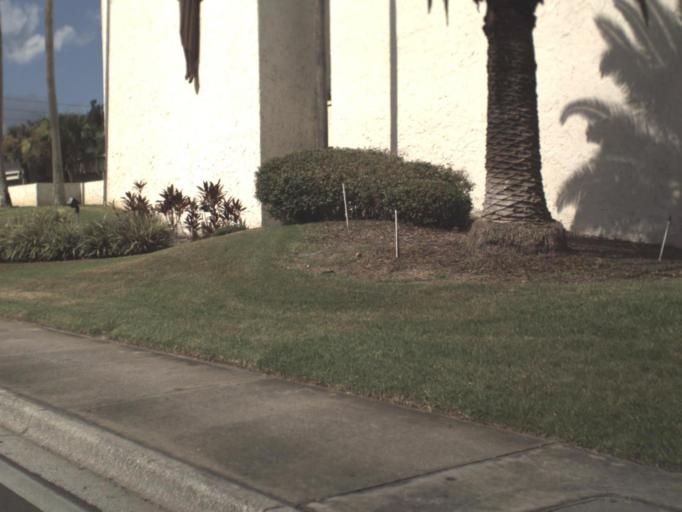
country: US
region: Florida
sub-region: Pinellas County
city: Largo
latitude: 27.9212
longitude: -82.7878
